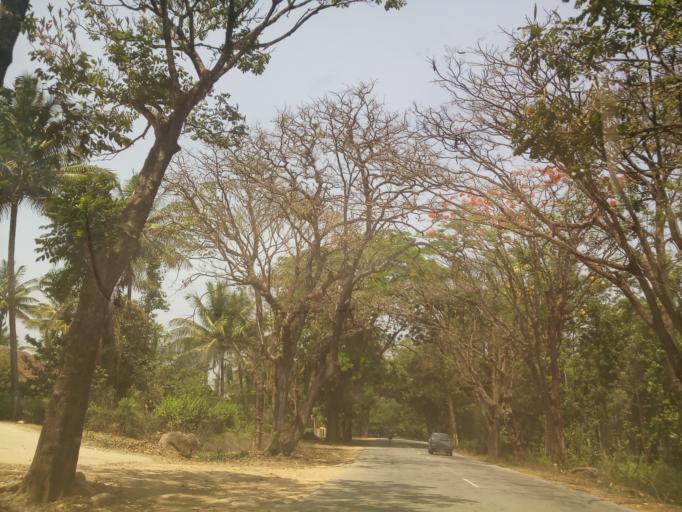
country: IN
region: Karnataka
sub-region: Hassan
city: Sakleshpur
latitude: 12.9552
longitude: 75.8513
